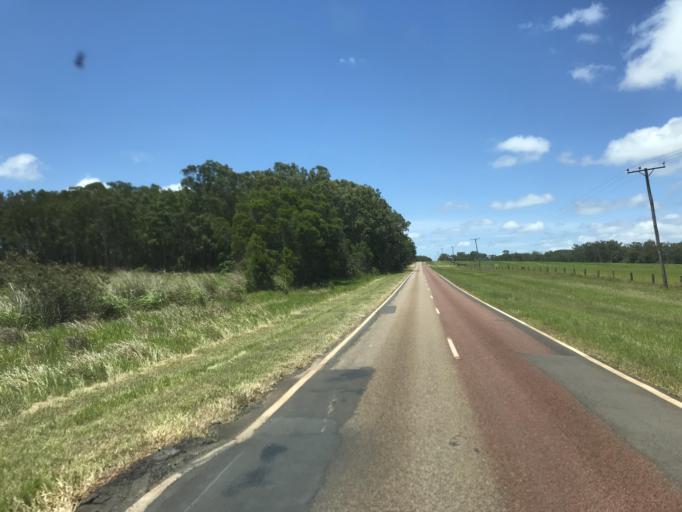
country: AU
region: Queensland
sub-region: Tablelands
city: Ravenshoe
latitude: -17.5257
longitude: 145.4536
